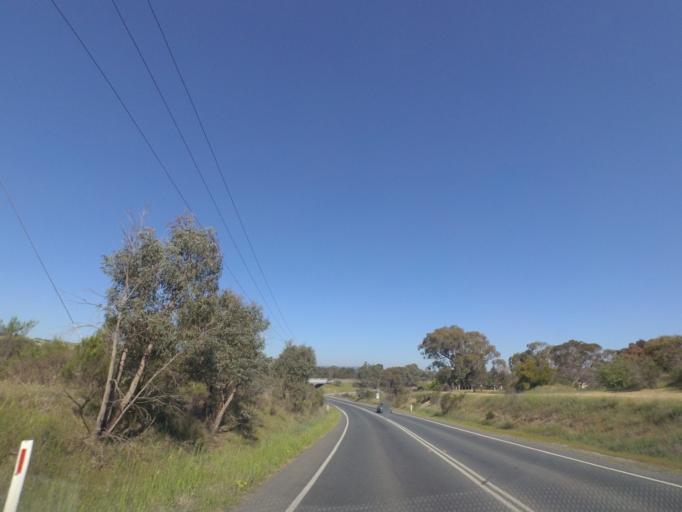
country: AU
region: Victoria
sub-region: Whittlesea
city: Whittlesea
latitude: -37.3497
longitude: 145.0197
